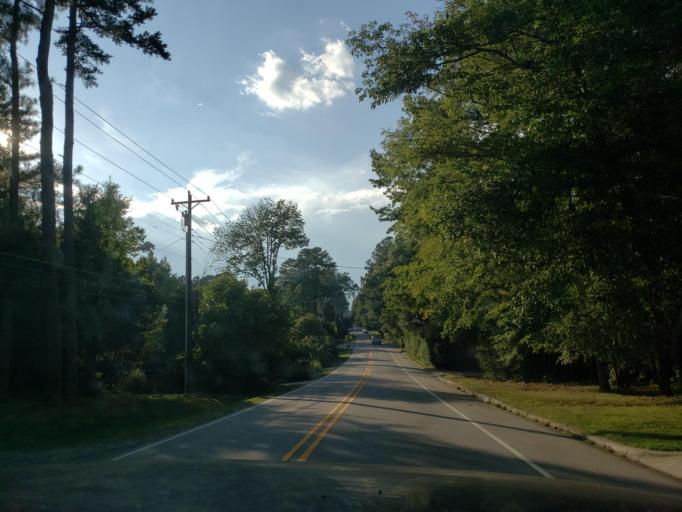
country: US
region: North Carolina
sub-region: Durham County
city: Durham
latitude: 35.9695
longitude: -78.9263
